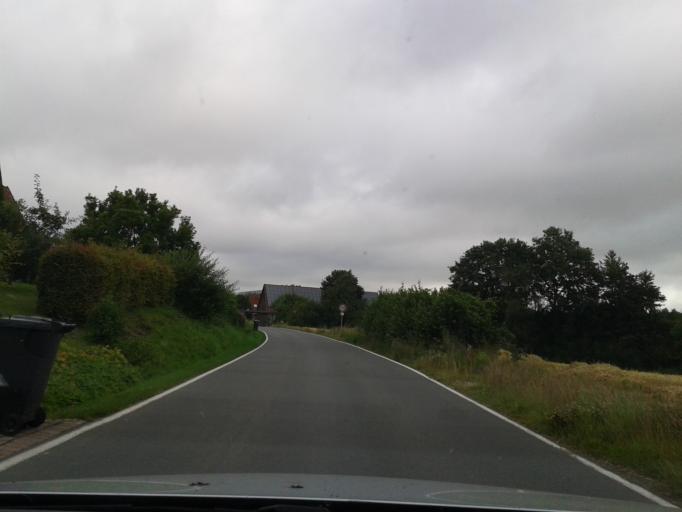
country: DE
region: North Rhine-Westphalia
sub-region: Regierungsbezirk Detmold
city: Barntrup
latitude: 52.0102
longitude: 9.0595
